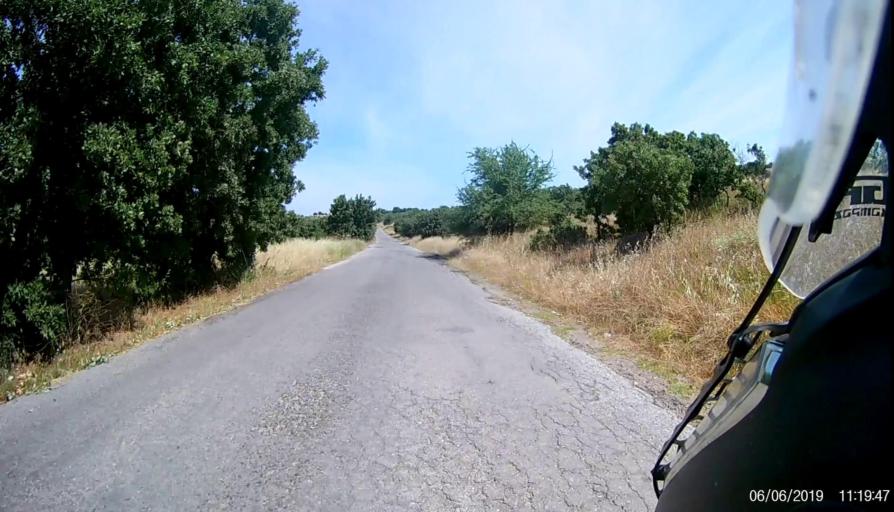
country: TR
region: Canakkale
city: Gulpinar
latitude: 39.6602
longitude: 26.1641
